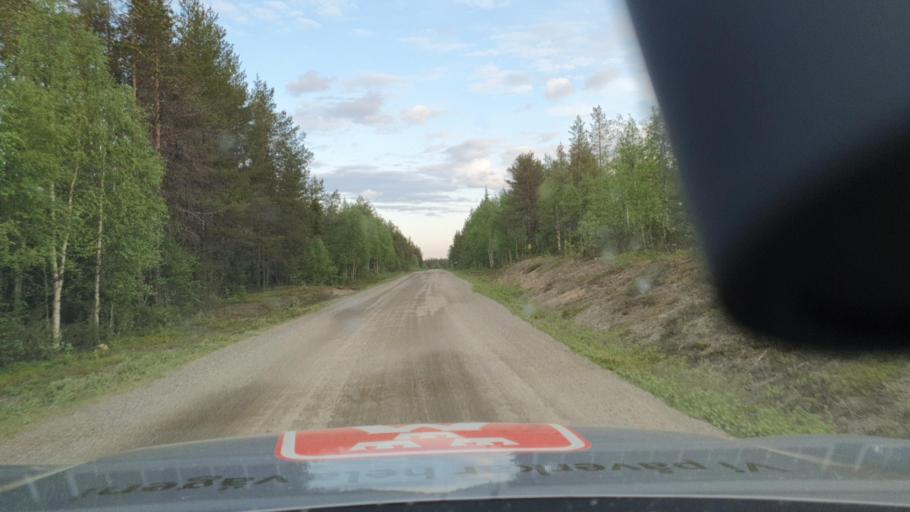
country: SE
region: Norrbotten
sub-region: Bodens Kommun
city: Boden
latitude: 66.6003
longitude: 21.3686
